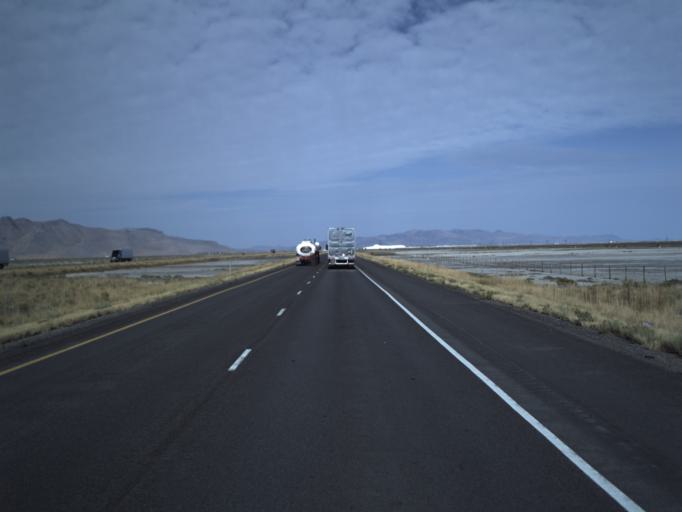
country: US
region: Utah
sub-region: Tooele County
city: Grantsville
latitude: 40.6936
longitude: -112.4686
